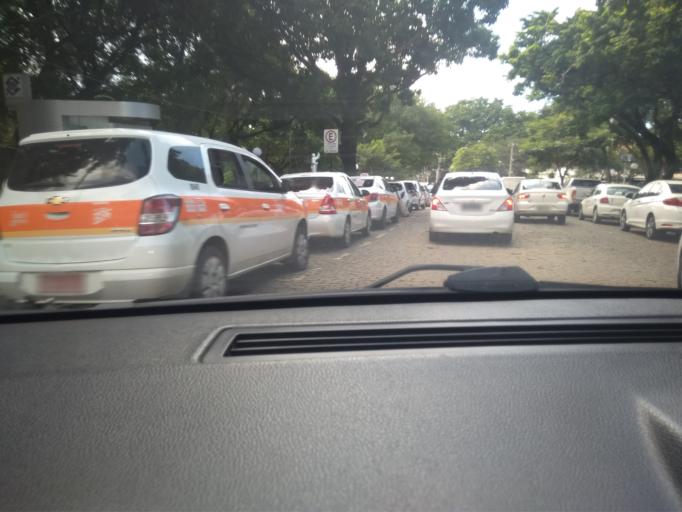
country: BR
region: Espirito Santo
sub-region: Vitoria
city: Vitoria
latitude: -20.2998
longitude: -40.3180
